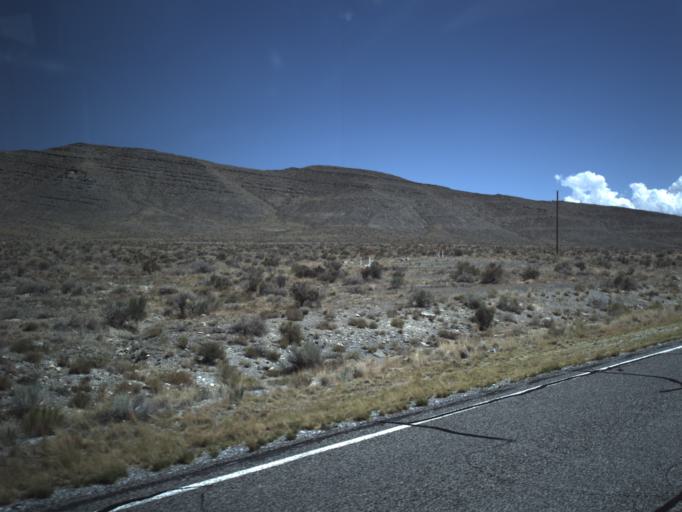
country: US
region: Utah
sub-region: Beaver County
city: Milford
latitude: 39.0294
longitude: -113.3799
